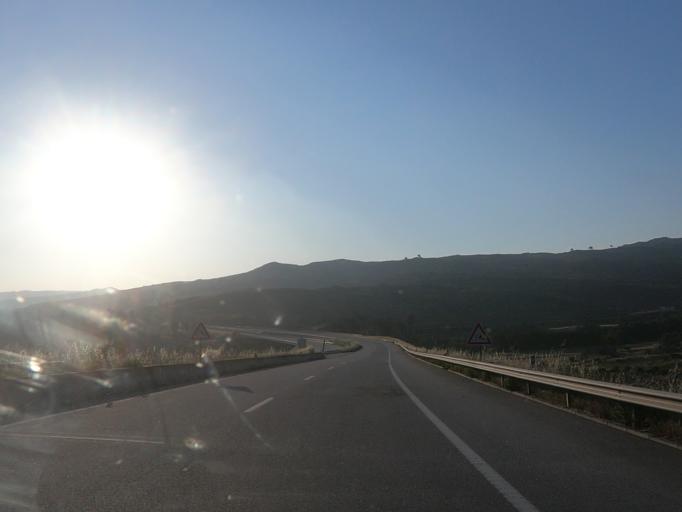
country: PT
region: Guarda
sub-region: Celorico da Beira
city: Celorico da Beira
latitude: 40.6299
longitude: -7.4292
